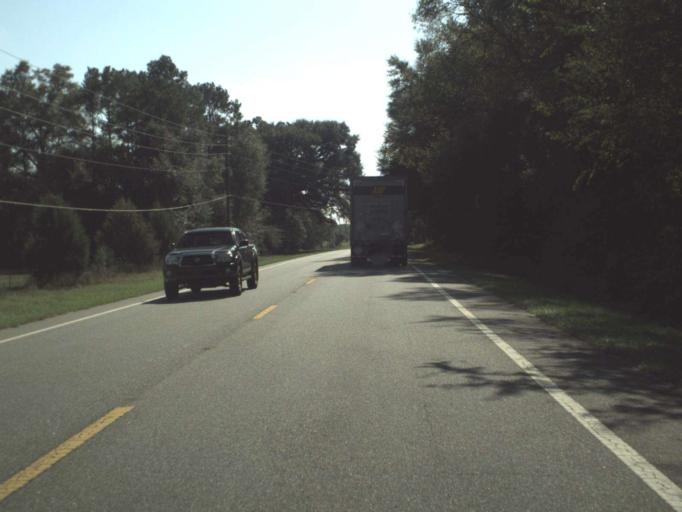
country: US
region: Florida
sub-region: Jackson County
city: Malone
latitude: 30.8934
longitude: -85.1612
